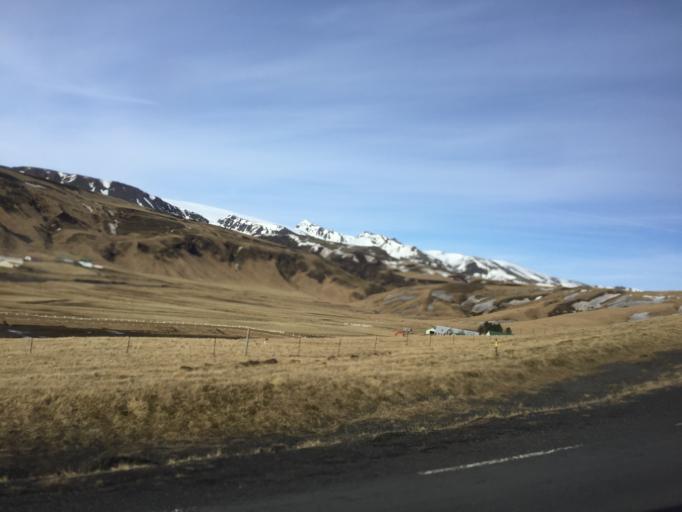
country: IS
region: South
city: Vestmannaeyjar
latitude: 63.4527
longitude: -19.0614
